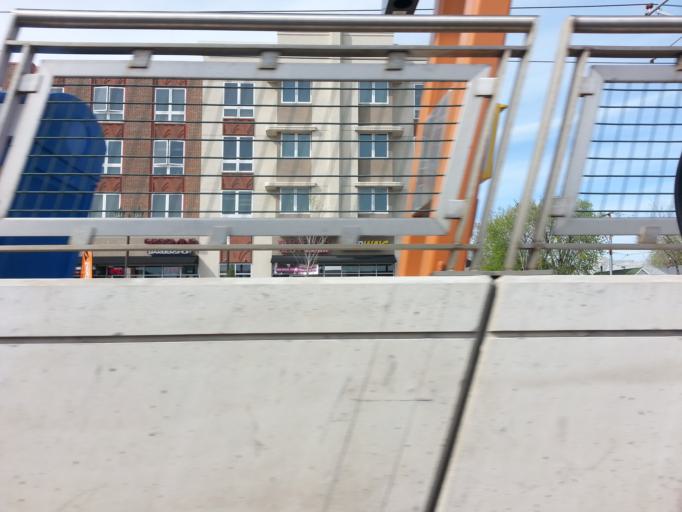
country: US
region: Minnesota
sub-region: Ramsey County
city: Saint Paul
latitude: 44.9557
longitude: -93.1254
